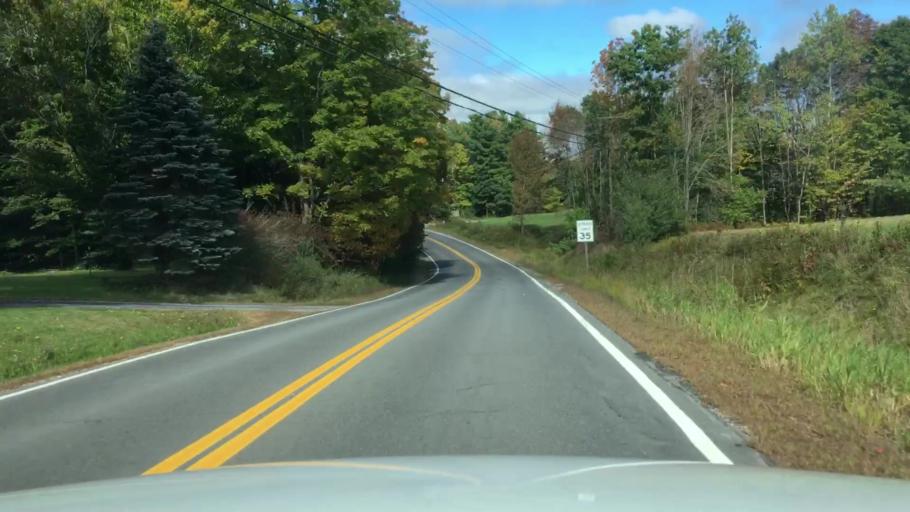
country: US
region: Maine
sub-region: Sagadahoc County
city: North Bath
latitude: 44.0020
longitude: -69.8903
